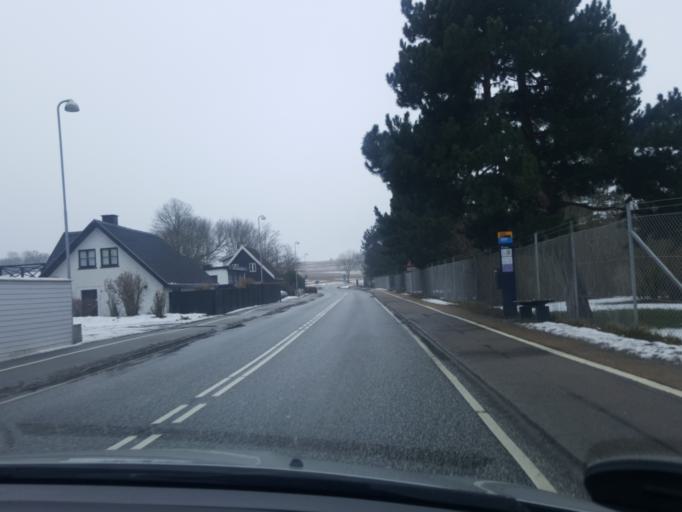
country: DK
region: Capital Region
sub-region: Horsholm Kommune
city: Horsholm
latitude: 55.8734
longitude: 12.4778
